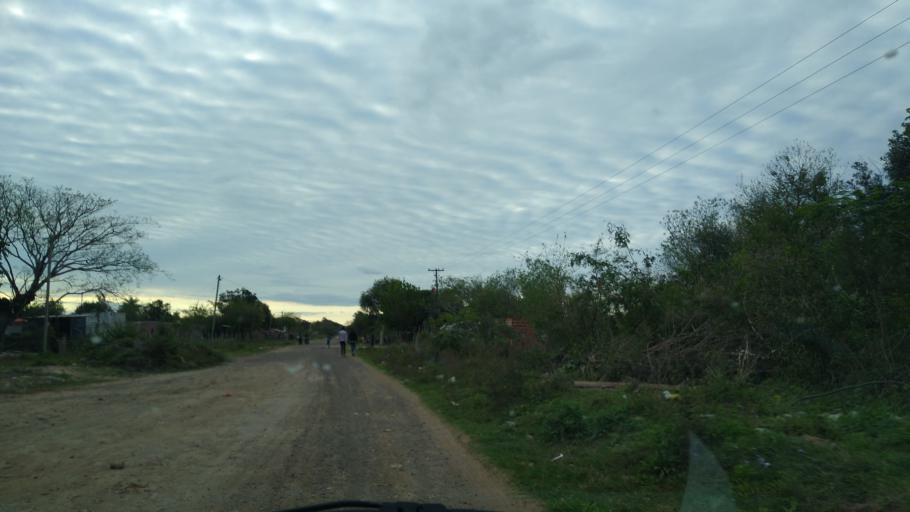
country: AR
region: Chaco
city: Fontana
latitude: -27.4013
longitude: -59.0426
